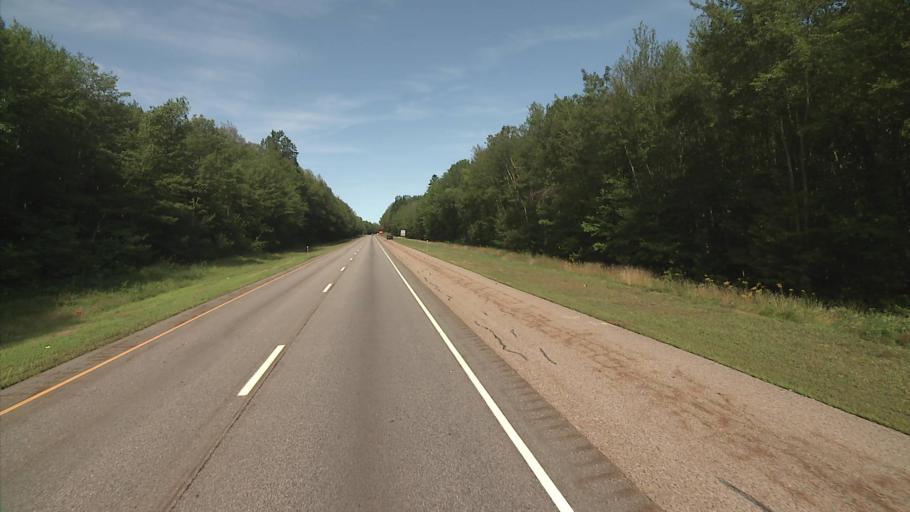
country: US
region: Connecticut
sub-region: New London County
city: Colchester
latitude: 41.5694
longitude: -72.2762
